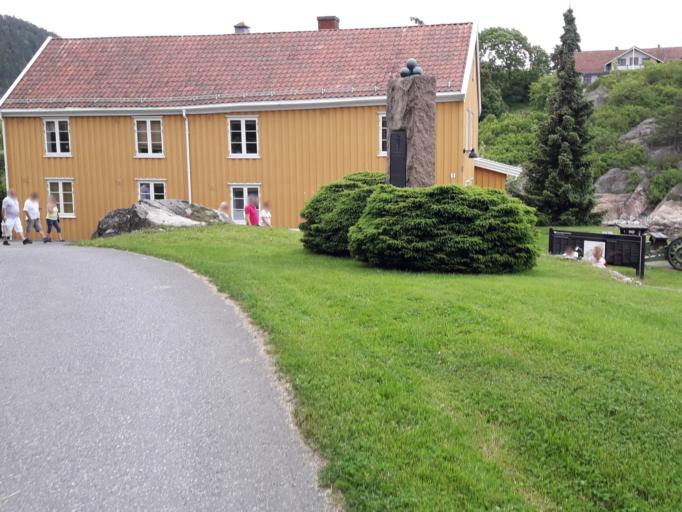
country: NO
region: Akershus
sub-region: Frogn
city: Drobak
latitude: 59.6761
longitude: 10.6067
